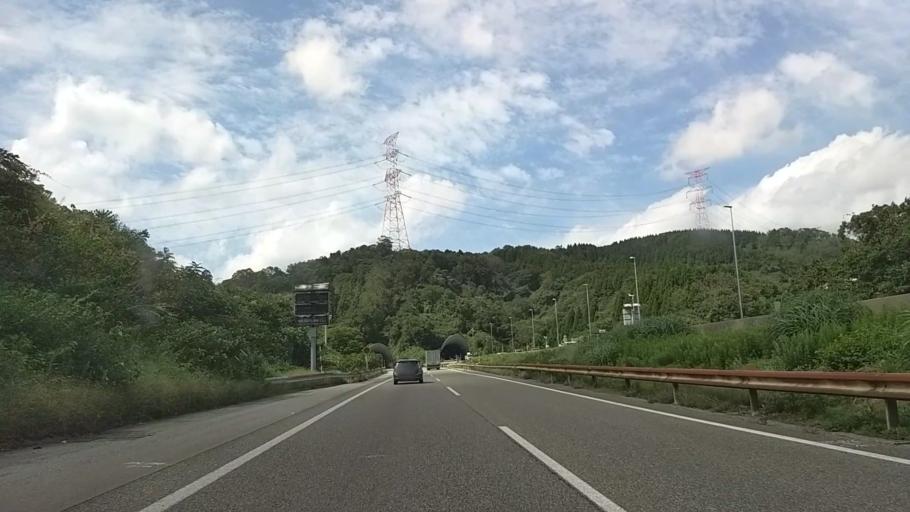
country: JP
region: Toyama
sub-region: Oyabe Shi
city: Oyabe
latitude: 36.6038
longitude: 136.7960
